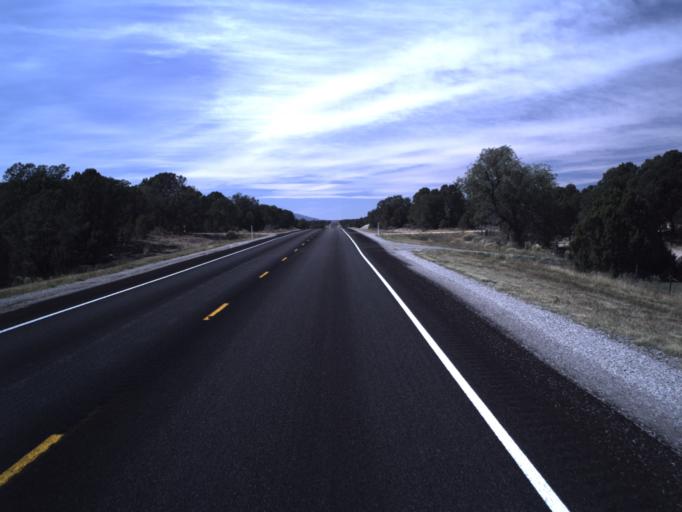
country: US
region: Colorado
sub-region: Dolores County
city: Dove Creek
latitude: 37.8297
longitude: -109.0880
